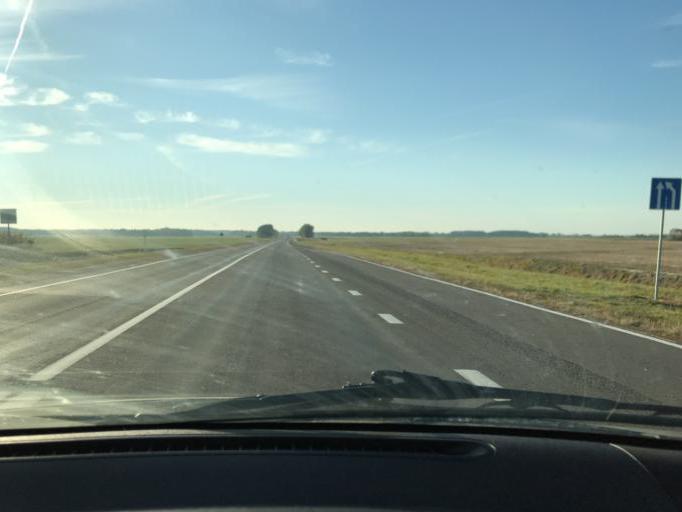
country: BY
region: Brest
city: Antopal'
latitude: 52.2072
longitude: 24.6007
